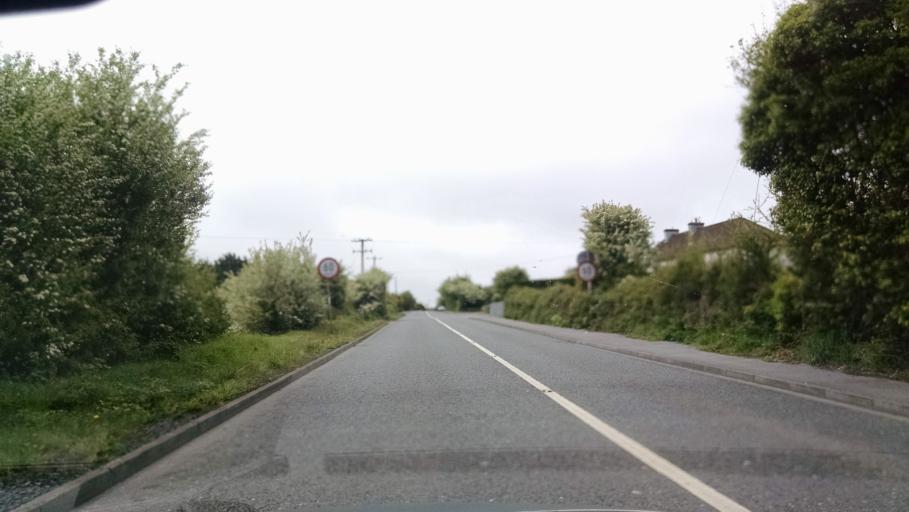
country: IE
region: Connaught
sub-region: County Galway
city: Gaillimh
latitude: 53.3051
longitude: -9.0333
